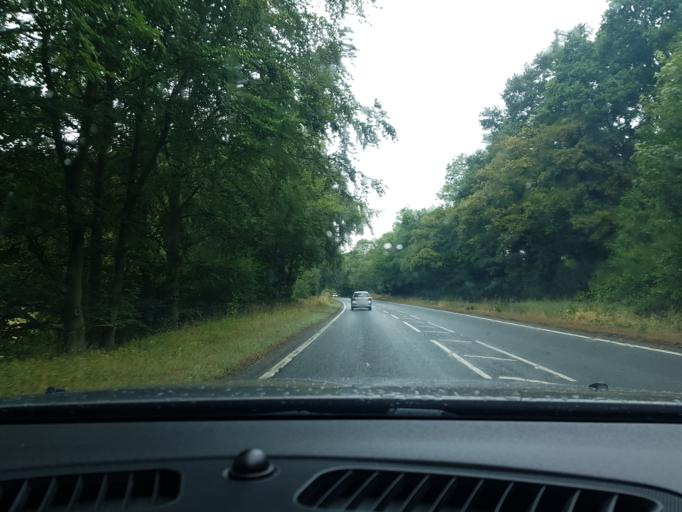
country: GB
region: England
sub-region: Hampshire
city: Odiham
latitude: 51.2546
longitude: -0.9139
